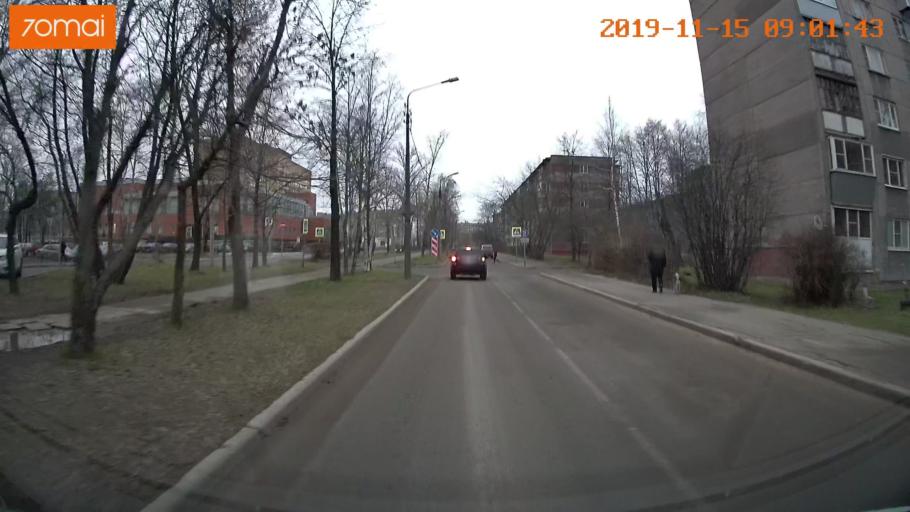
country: RU
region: Vologda
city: Cherepovets
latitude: 59.1338
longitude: 37.9266
